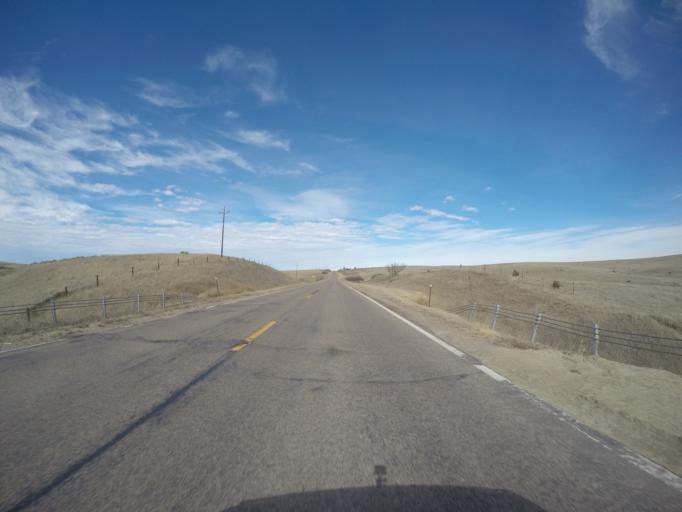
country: US
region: Nebraska
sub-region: Franklin County
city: Franklin
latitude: 40.1499
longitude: -98.9525
